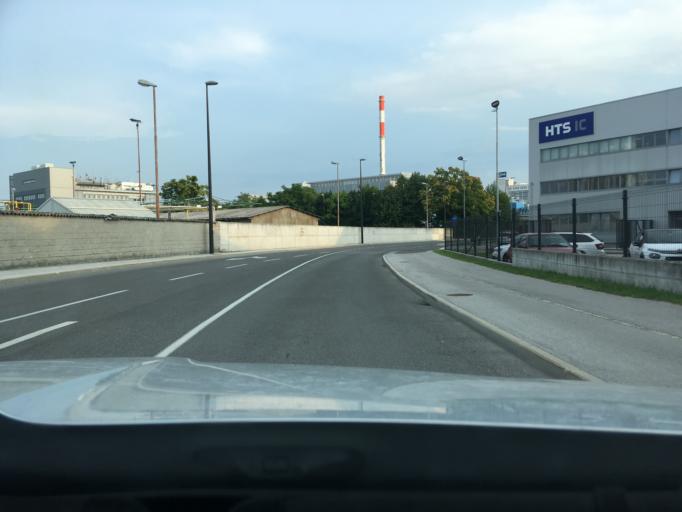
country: SI
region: Ljubljana
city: Ljubljana
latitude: 46.0813
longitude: 14.4982
